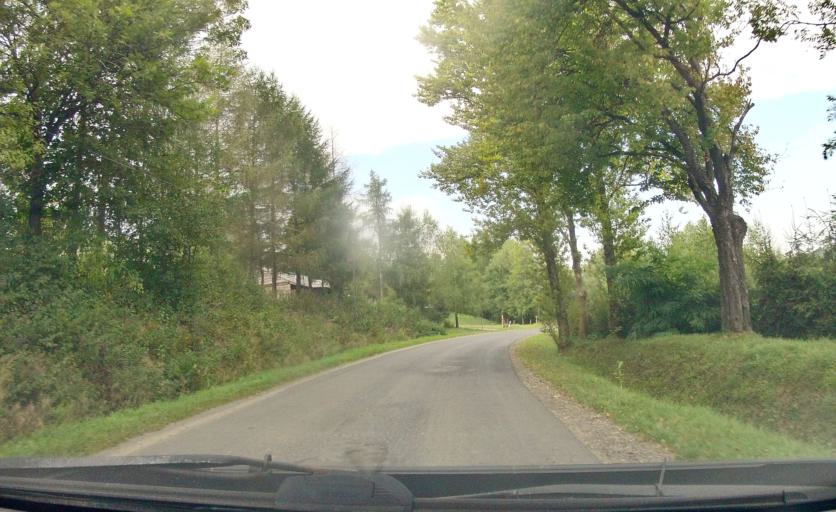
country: PL
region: Subcarpathian Voivodeship
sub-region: Powiat krosnienski
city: Dukla
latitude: 49.5243
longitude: 21.6151
